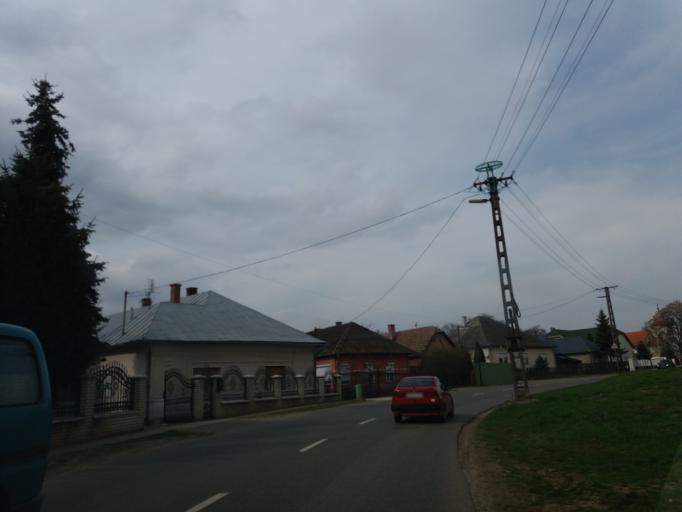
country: HU
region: Szabolcs-Szatmar-Bereg
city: Anarcs
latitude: 48.1725
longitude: 22.0965
